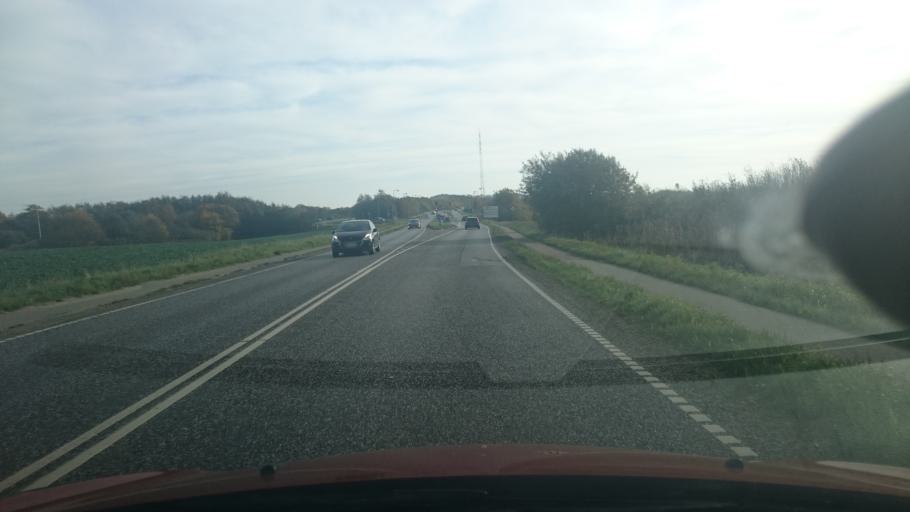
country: DK
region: Central Jutland
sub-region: Randers Kommune
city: Assentoft
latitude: 56.4408
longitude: 10.1116
